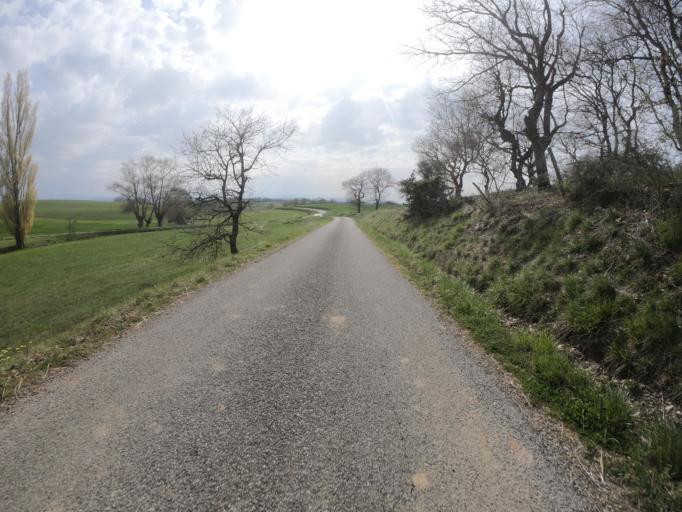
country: FR
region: Languedoc-Roussillon
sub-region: Departement de l'Aude
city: Belpech
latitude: 43.1545
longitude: 1.7770
